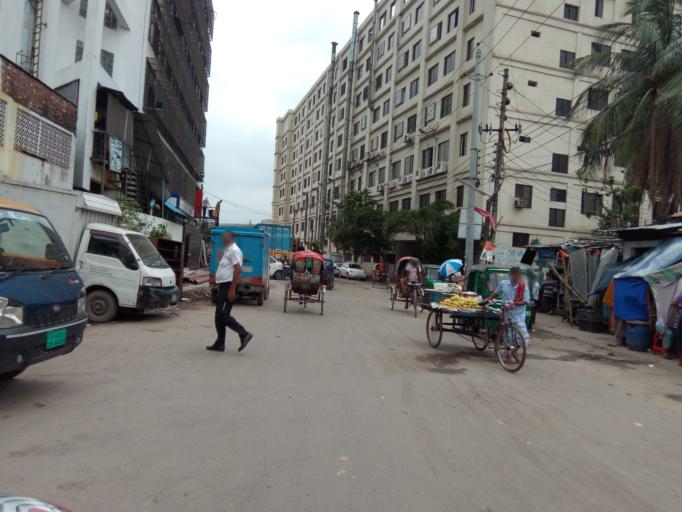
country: BD
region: Dhaka
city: Paltan
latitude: 23.7617
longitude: 90.4048
